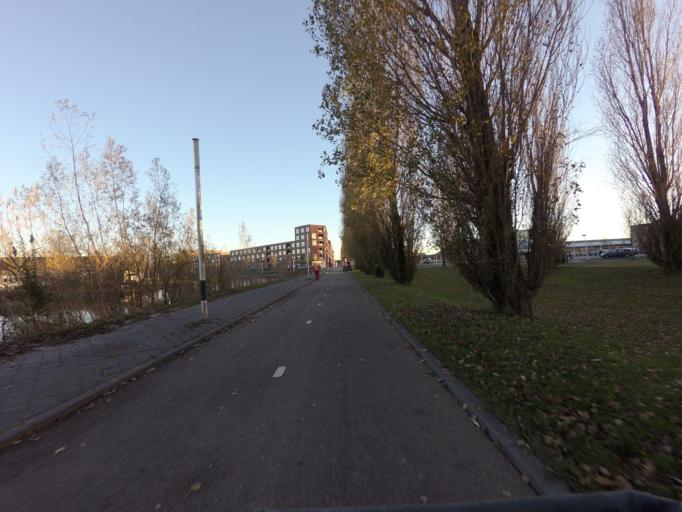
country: NL
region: Utrecht
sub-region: Stichtse Vecht
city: Maarssen
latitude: 52.1030
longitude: 5.0470
